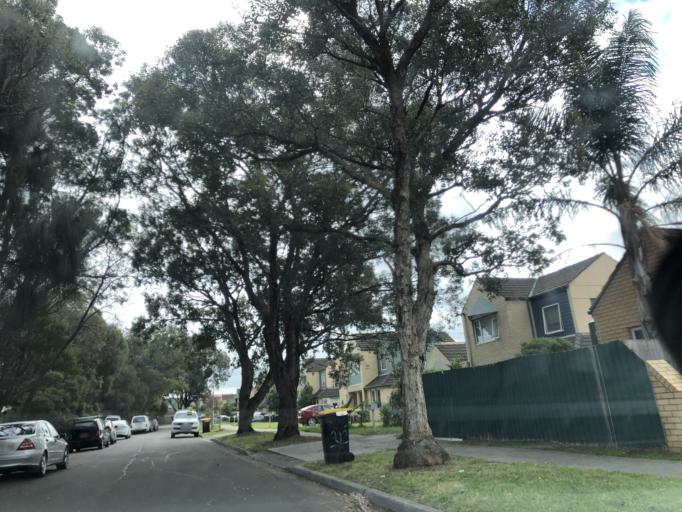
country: AU
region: Victoria
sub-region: Kingston
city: Clayton South
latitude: -37.9359
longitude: 145.1082
